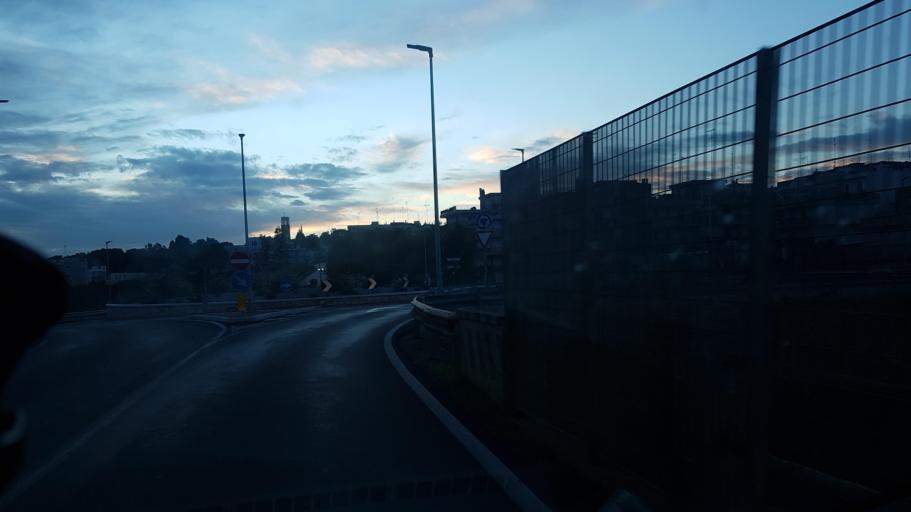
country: IT
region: Apulia
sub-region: Provincia di Brindisi
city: Ceglie Messapica
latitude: 40.6427
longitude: 17.5233
